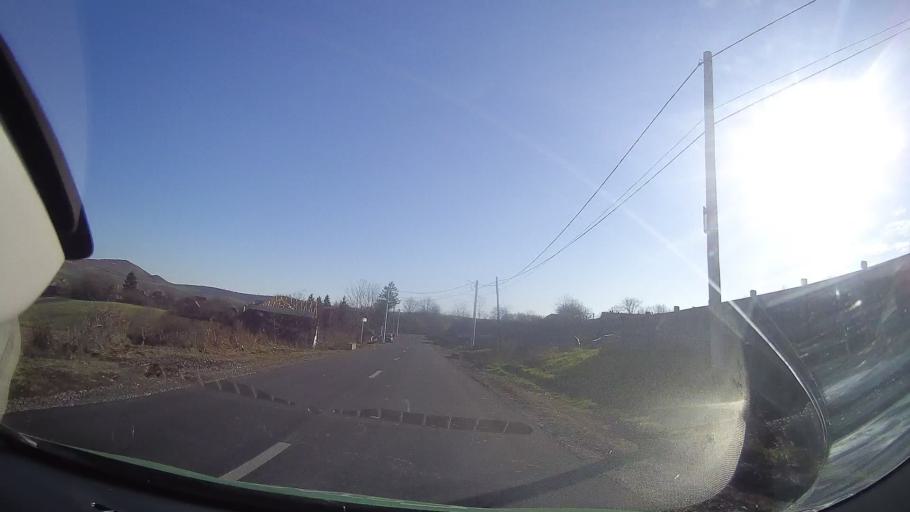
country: RO
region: Mures
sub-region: Comuna Band
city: Band
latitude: 46.5810
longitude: 24.3625
